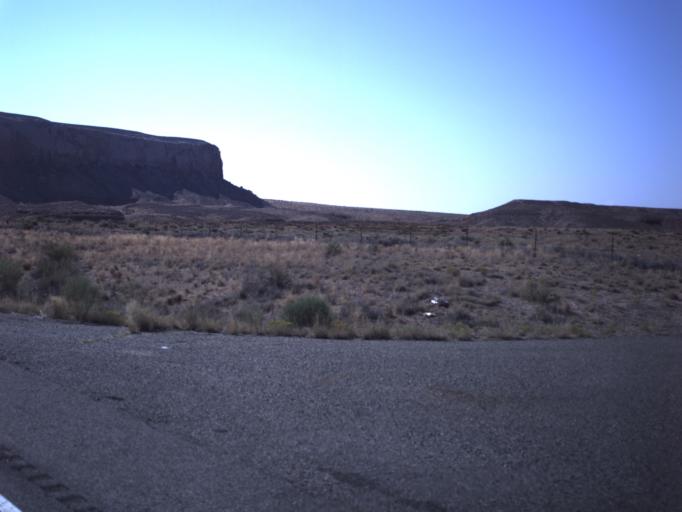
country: US
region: Utah
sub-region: San Juan County
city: Blanding
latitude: 37.2486
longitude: -109.6104
